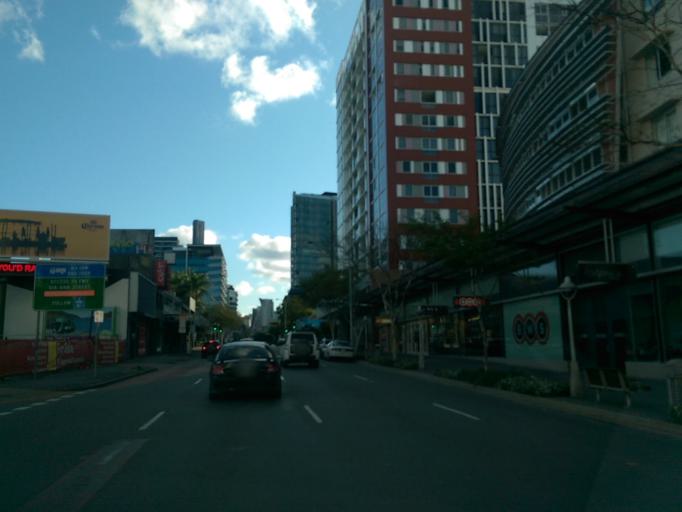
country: AU
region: Queensland
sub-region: Brisbane
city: Fortitude Valley
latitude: -27.4535
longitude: 153.0399
